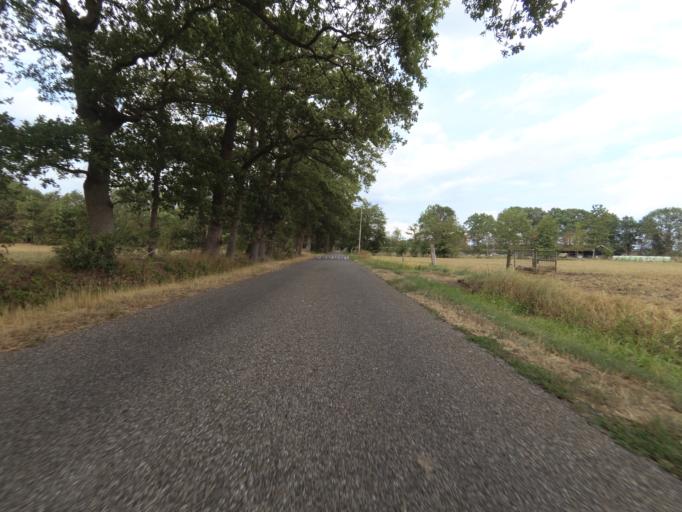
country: NL
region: Overijssel
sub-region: Gemeente Hof van Twente
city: Delden
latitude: 52.2278
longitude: 6.7458
